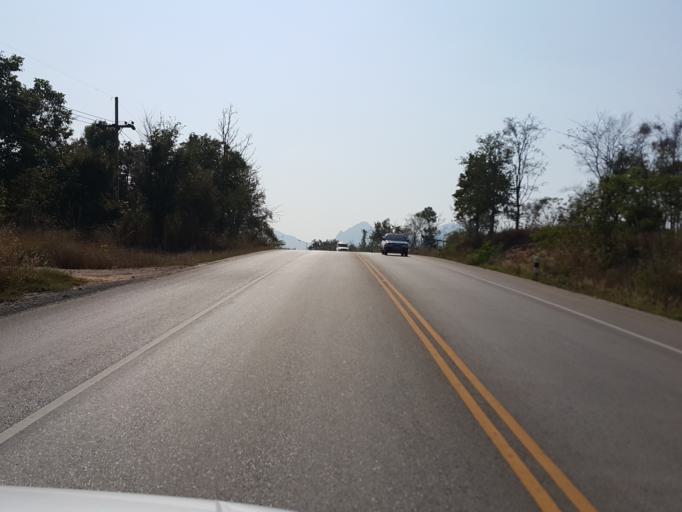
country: TH
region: Lampang
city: Chae Hom
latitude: 18.7793
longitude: 99.5830
